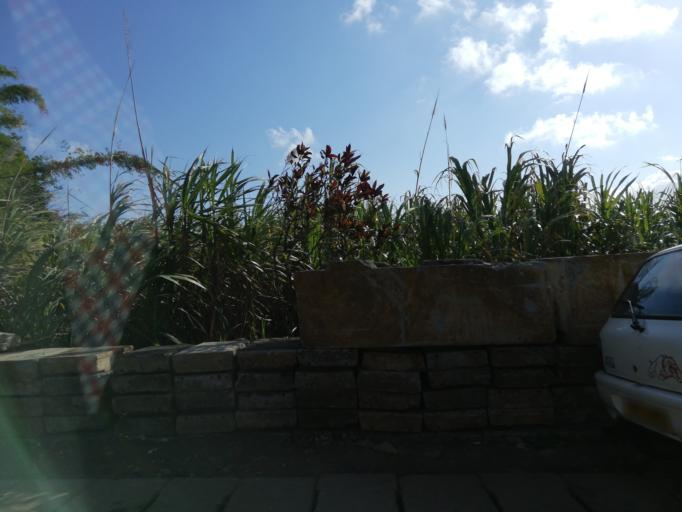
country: MU
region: Moka
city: Verdun
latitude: -20.2253
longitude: 57.5367
